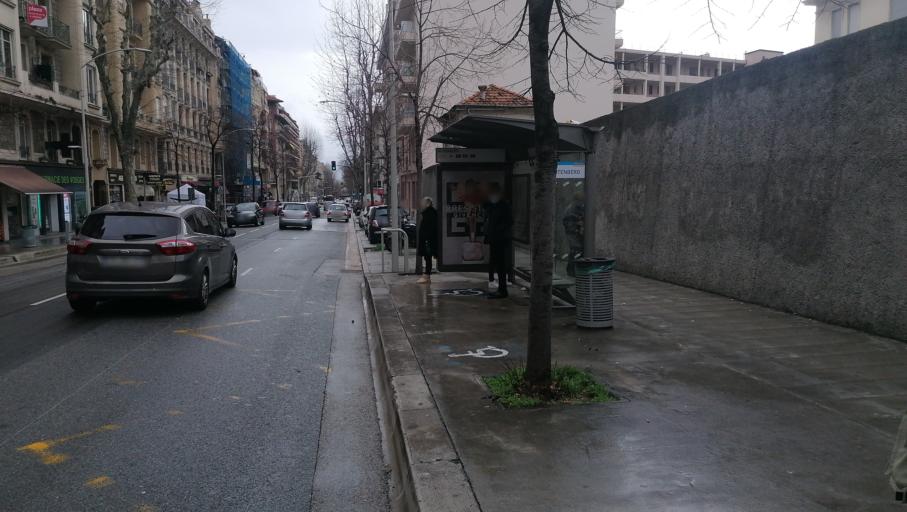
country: FR
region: Provence-Alpes-Cote d'Azur
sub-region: Departement des Alpes-Maritimes
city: Nice
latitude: 43.7093
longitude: 7.2560
